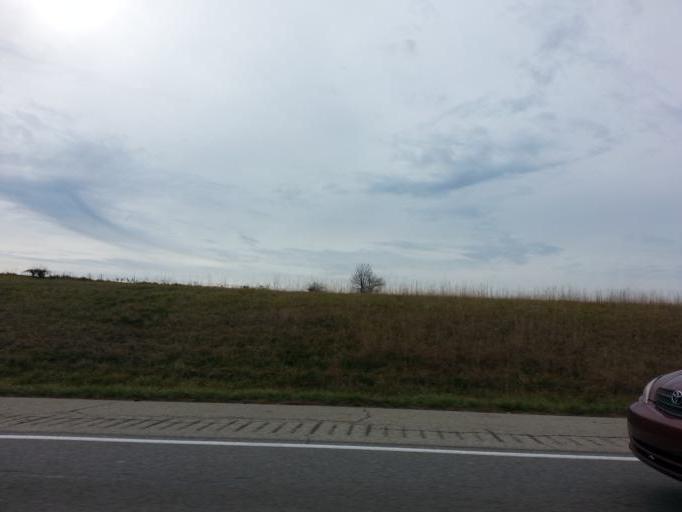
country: US
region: Indiana
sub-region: Decatur County
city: Greensburg
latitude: 39.3489
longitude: -85.4422
